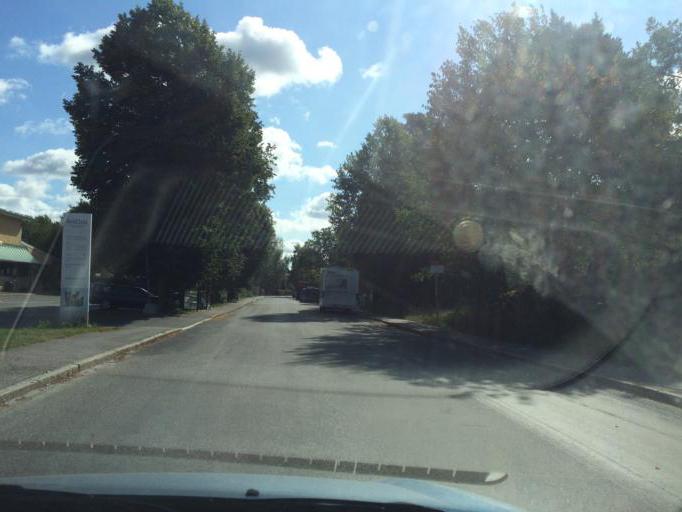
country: SE
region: Stockholm
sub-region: Nacka Kommun
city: Nacka
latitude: 59.2776
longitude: 18.1408
